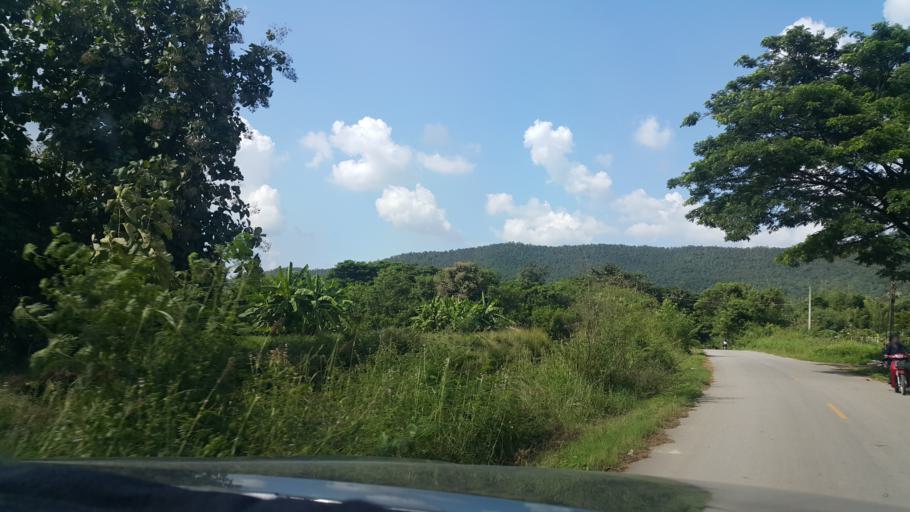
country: TH
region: Chiang Mai
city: Mae On
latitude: 18.7372
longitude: 99.2030
